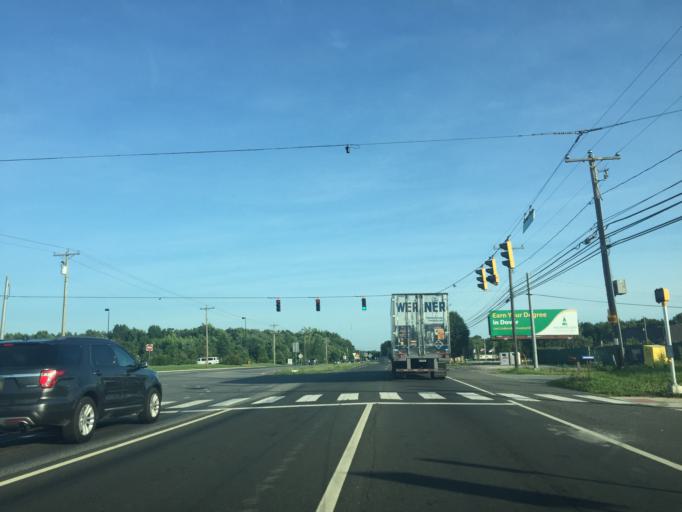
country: US
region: Delaware
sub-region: Kent County
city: Cheswold
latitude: 39.2177
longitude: -75.5738
